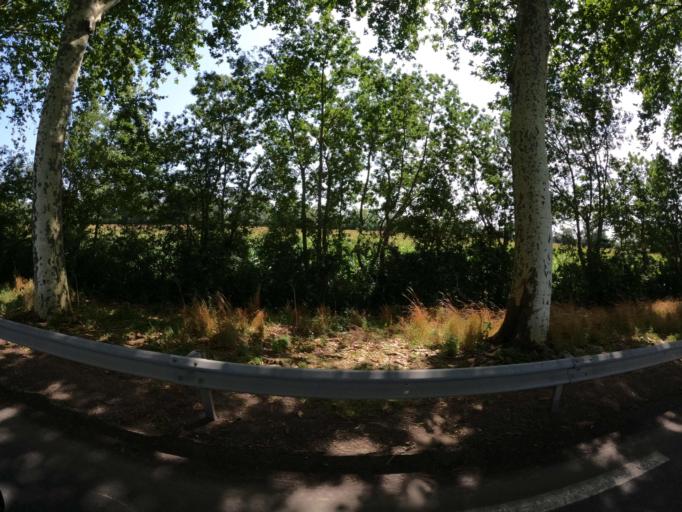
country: FR
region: Poitou-Charentes
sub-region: Departement des Deux-Sevres
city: Frontenay-Rohan-Rohan
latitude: 46.2758
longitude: -0.5250
